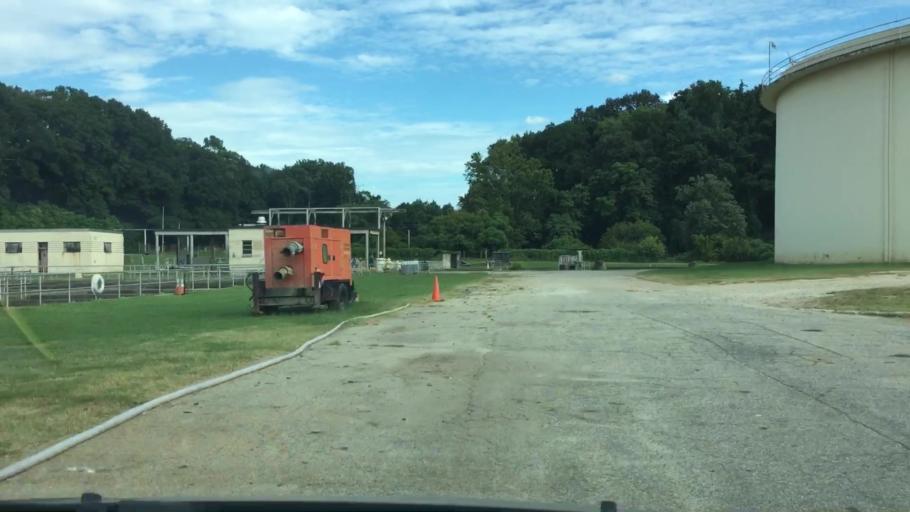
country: US
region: Georgia
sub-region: DeKalb County
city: Gresham Park
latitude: 33.7029
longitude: -84.3348
